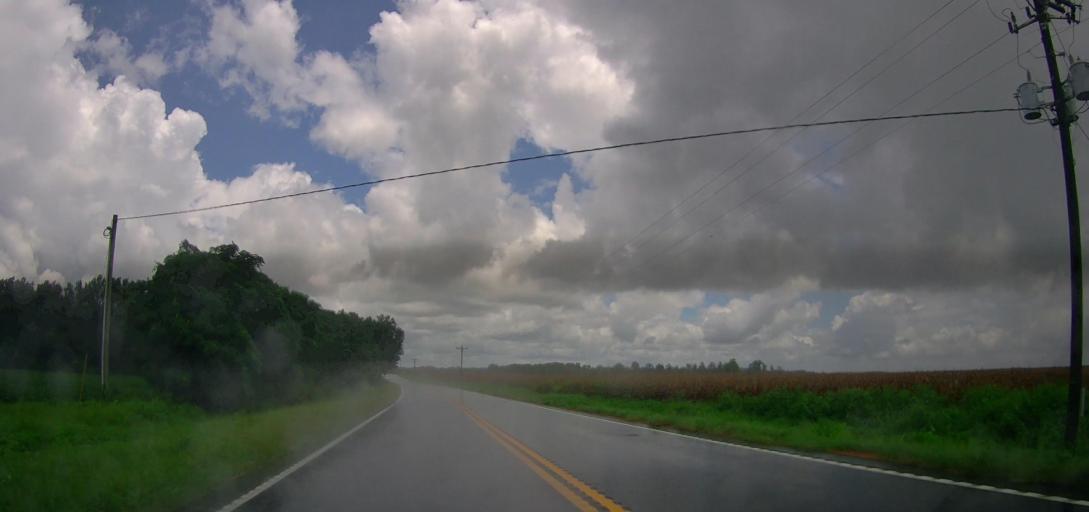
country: US
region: Georgia
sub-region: Pulaski County
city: Hawkinsville
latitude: 32.1933
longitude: -83.5179
